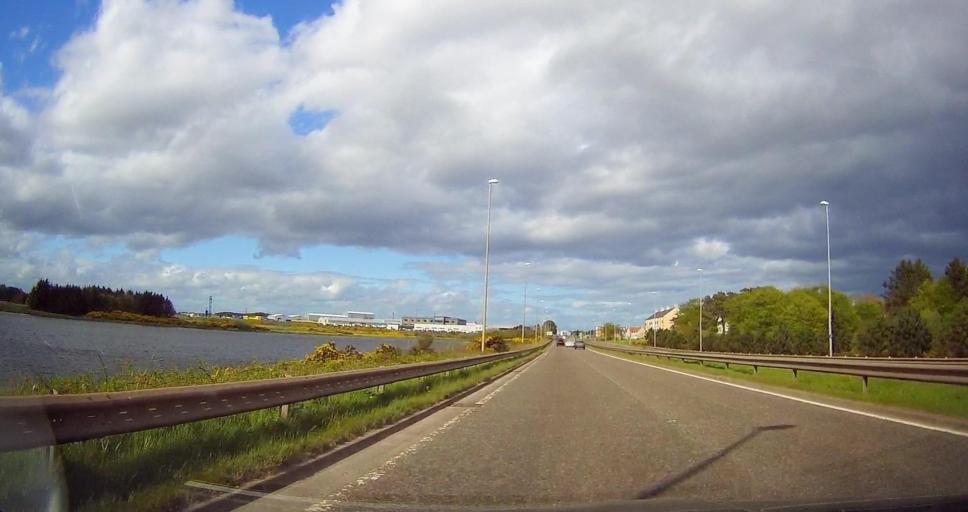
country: GB
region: Scotland
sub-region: Aberdeen City
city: Aberdeen
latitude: 57.1000
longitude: -2.1011
